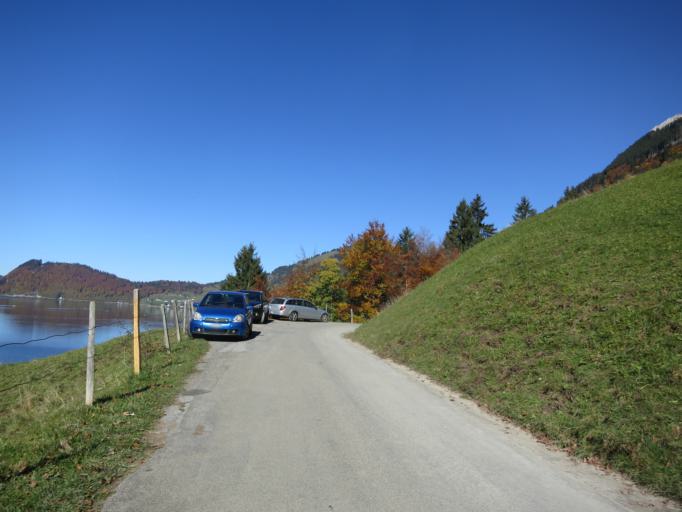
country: CH
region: Schwyz
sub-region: Bezirk March
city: Vorderthal
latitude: 47.0768
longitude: 8.9256
